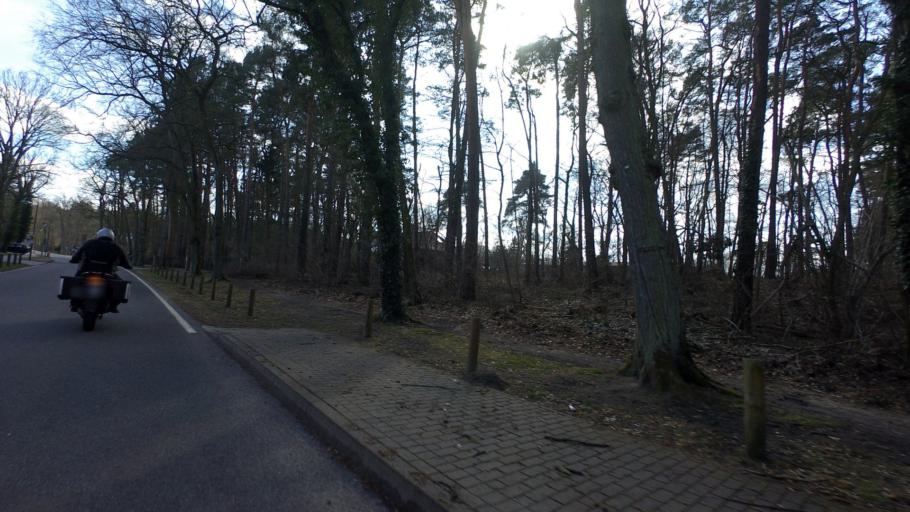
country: DE
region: Brandenburg
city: Biesenthal
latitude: 52.7732
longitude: 13.6143
